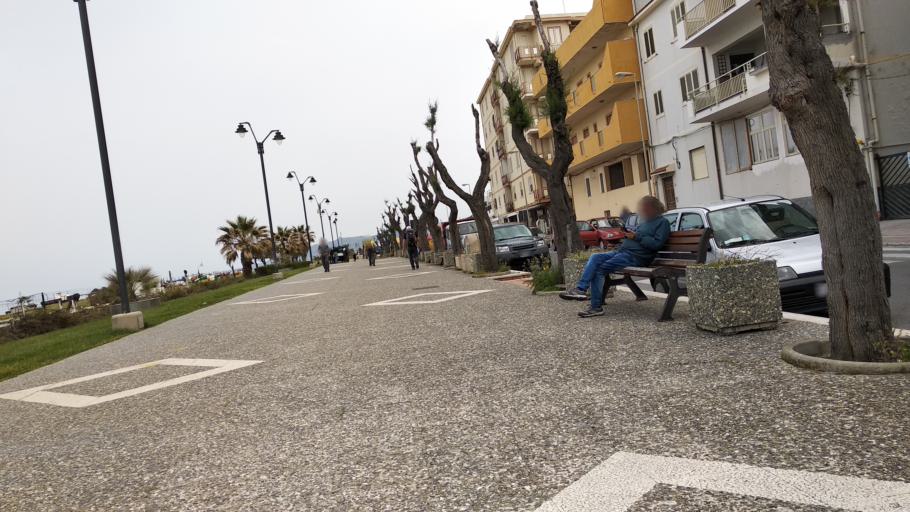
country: IT
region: Sicily
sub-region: Messina
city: Venetico Marina
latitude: 38.2217
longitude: 15.3690
